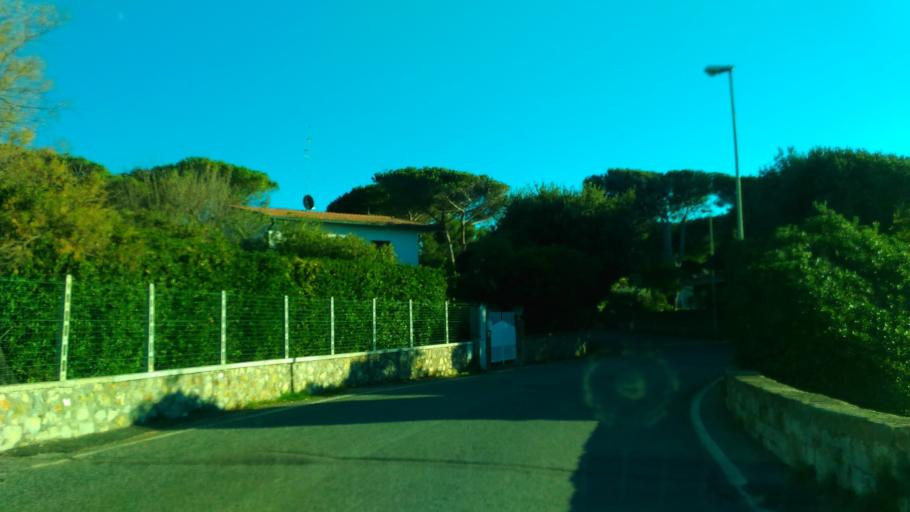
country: IT
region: Tuscany
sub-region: Provincia di Livorno
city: Quercianella
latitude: 43.4508
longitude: 10.3761
